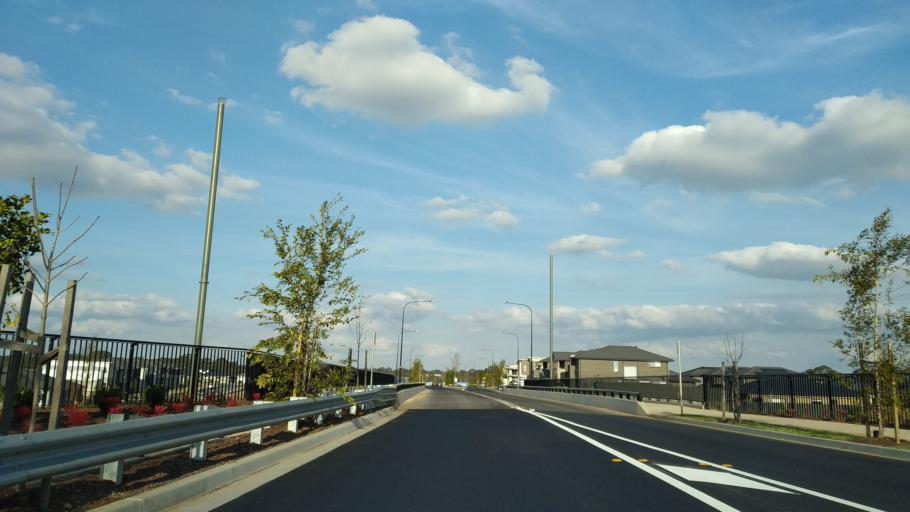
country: AU
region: New South Wales
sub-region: Penrith Municipality
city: Werrington County
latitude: -33.7343
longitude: 150.7511
